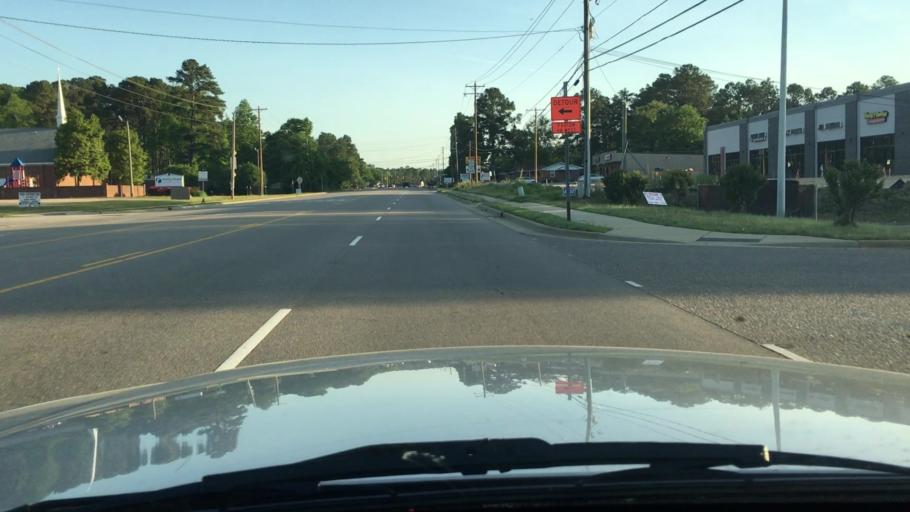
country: US
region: North Carolina
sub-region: Cumberland County
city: Fort Bragg
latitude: 35.0946
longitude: -79.0109
